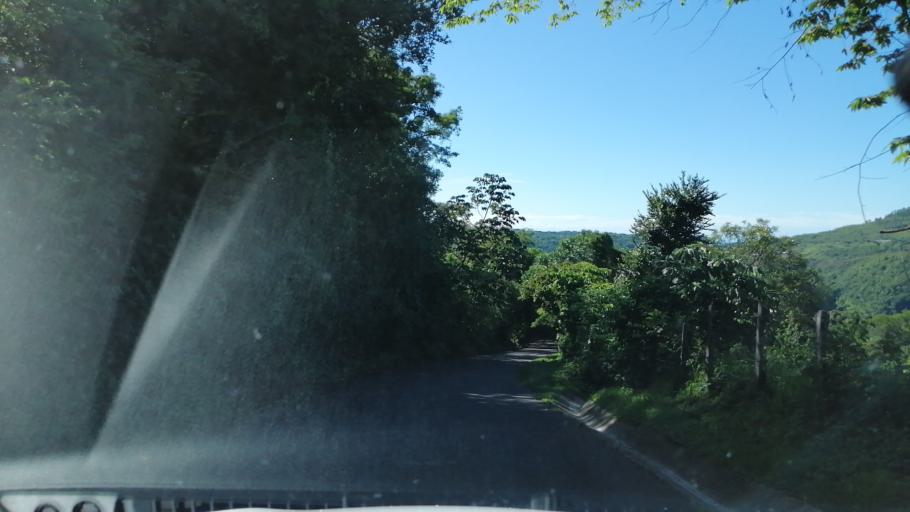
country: SV
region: Morazan
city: Corinto
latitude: 13.8112
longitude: -87.9910
